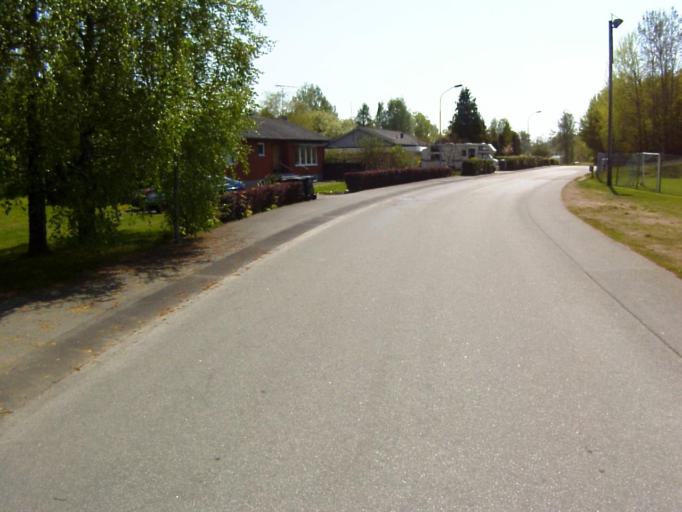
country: SE
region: Skane
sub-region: Kristianstads Kommun
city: Tollarp
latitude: 56.1714
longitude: 14.2903
